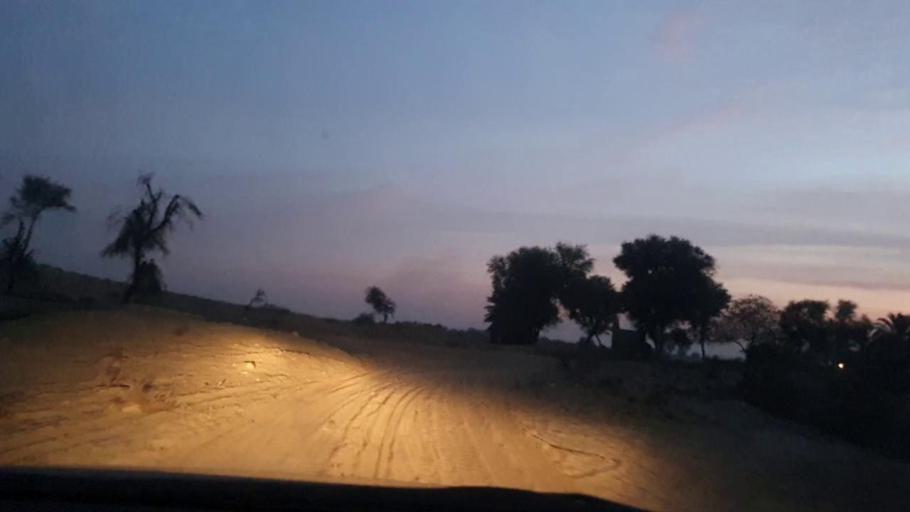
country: PK
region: Sindh
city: Sakrand
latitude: 26.1812
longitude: 68.3081
